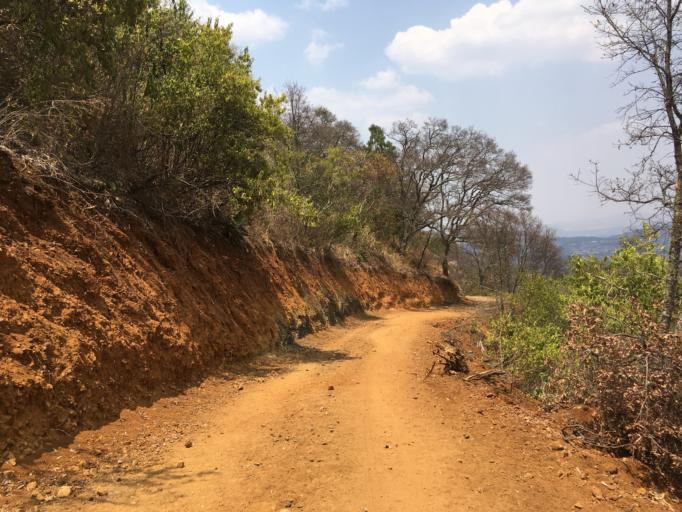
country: MX
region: Michoacan
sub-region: Patzcuaro
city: Santa Ana Chapitiro
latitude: 19.5094
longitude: -101.6403
